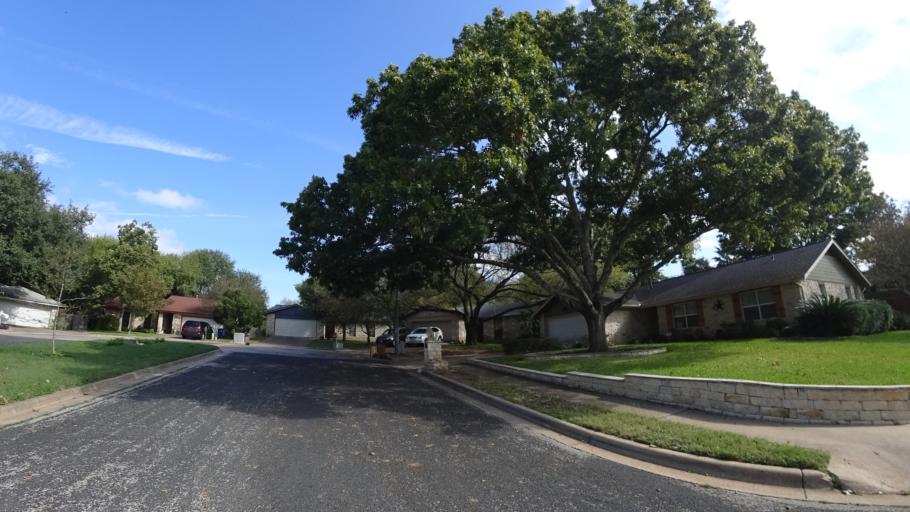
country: US
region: Texas
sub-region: Travis County
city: Shady Hollow
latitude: 30.1922
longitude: -97.8161
